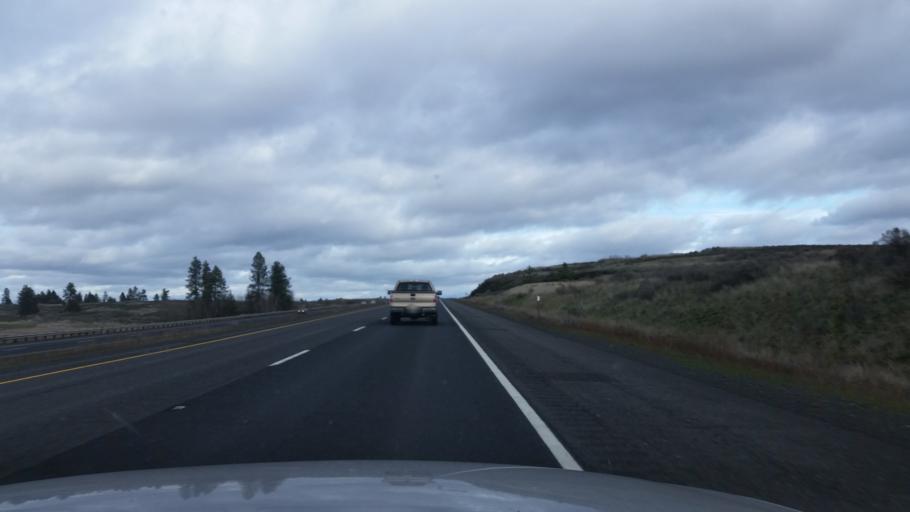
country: US
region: Washington
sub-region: Spokane County
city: Medical Lake
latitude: 47.3784
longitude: -117.8683
